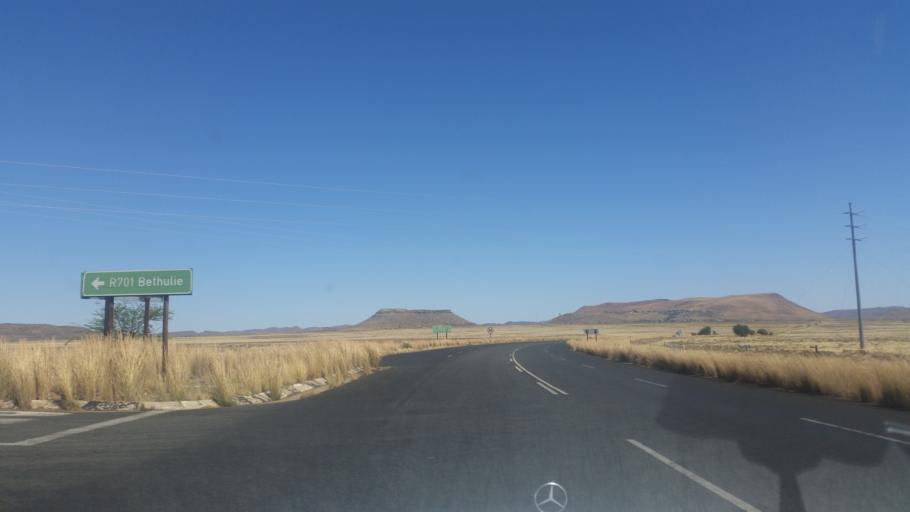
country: ZA
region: Northern Cape
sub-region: Pixley ka Seme District Municipality
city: Colesberg
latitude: -30.5559
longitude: 25.4974
